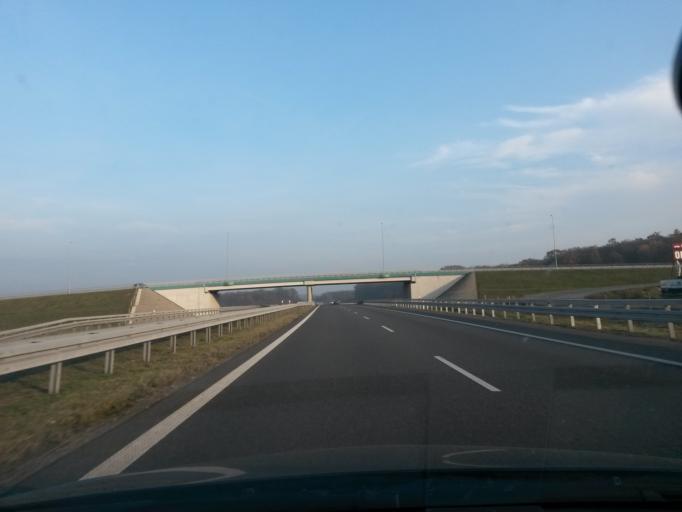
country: PL
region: Lower Silesian Voivodeship
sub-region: Powiat olesnicki
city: Sycow
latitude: 51.2937
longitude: 17.7120
